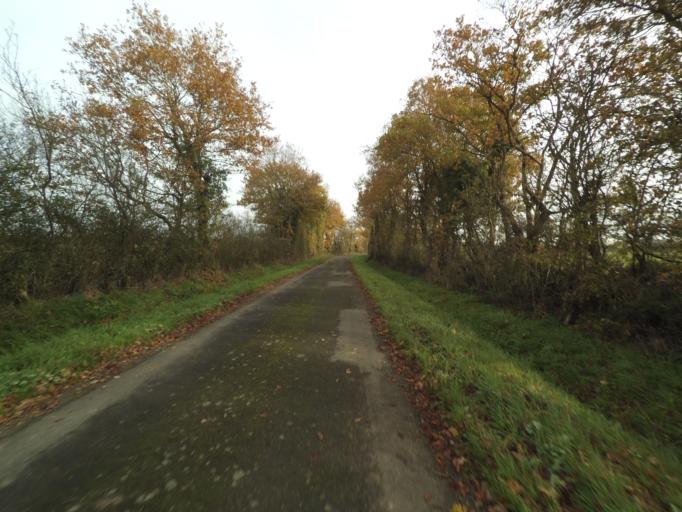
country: FR
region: Pays de la Loire
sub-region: Departement de la Loire-Atlantique
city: La Planche
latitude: 47.0138
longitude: -1.4074
